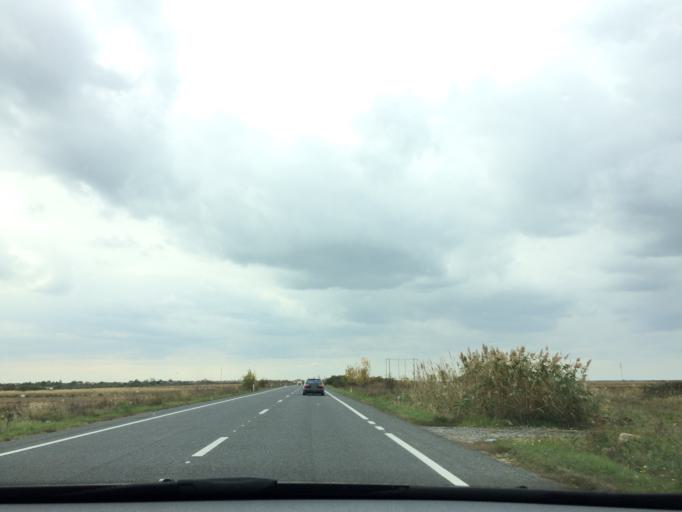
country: RO
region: Timis
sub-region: Oras Recas
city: Recas
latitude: 45.8006
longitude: 21.4879
